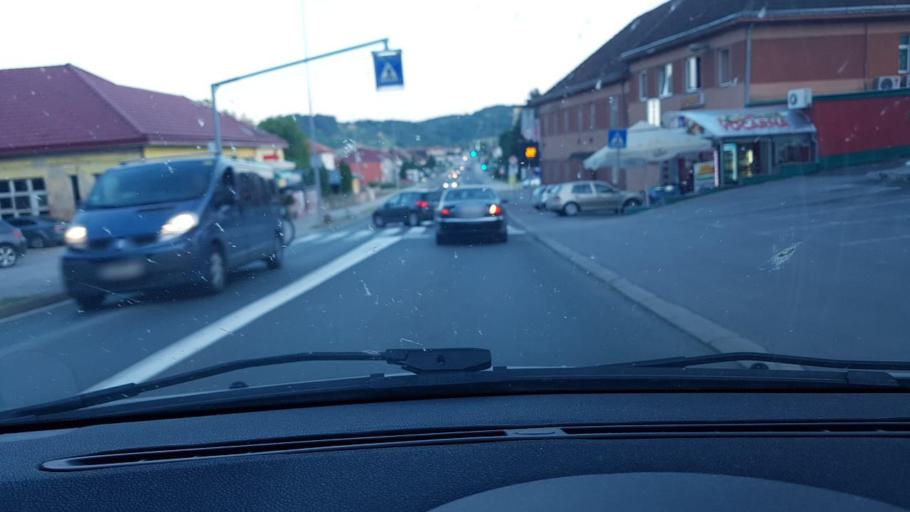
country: HR
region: Varazdinska
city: Remetinec
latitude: 46.1650
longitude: 16.3348
